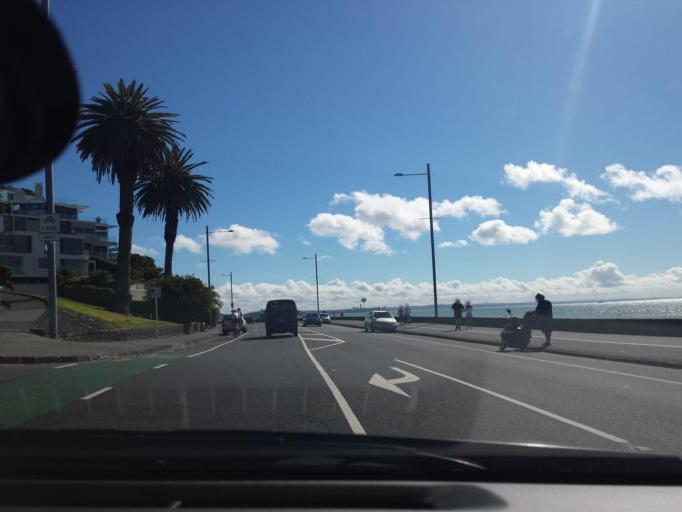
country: NZ
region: Auckland
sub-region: Auckland
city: Tamaki
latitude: -36.8505
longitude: 174.8522
